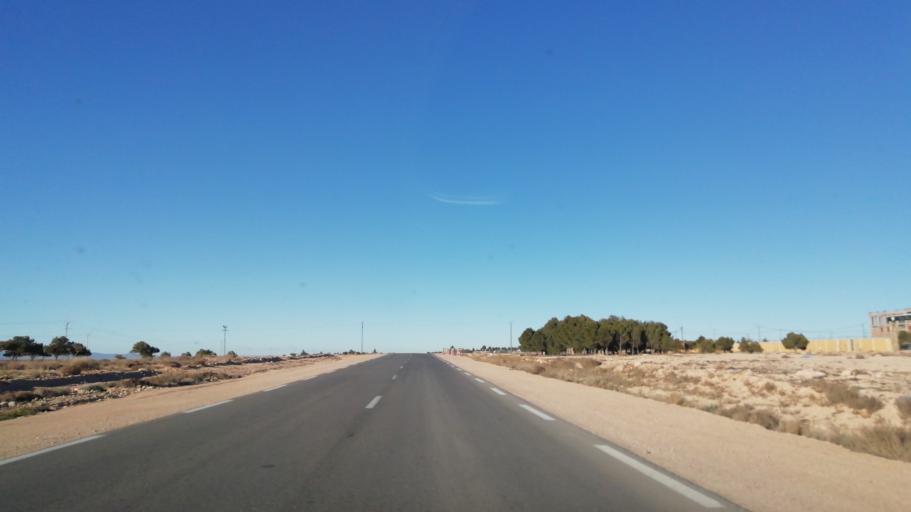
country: DZ
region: Tlemcen
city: Sebdou
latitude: 34.2651
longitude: -1.2582
